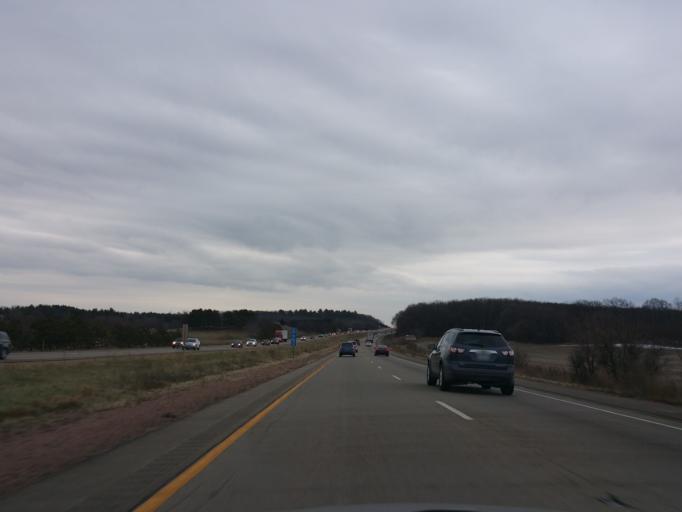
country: US
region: Wisconsin
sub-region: Sauk County
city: Baraboo
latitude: 43.5485
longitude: -89.6597
